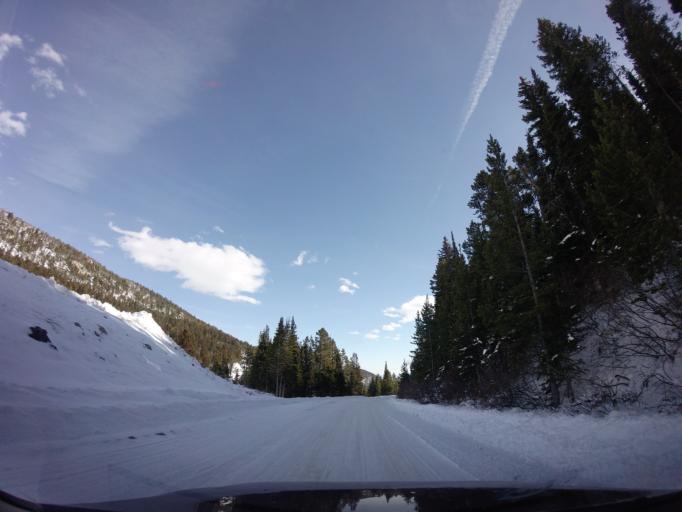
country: US
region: Montana
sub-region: Carbon County
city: Red Lodge
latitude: 45.1899
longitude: -109.3342
